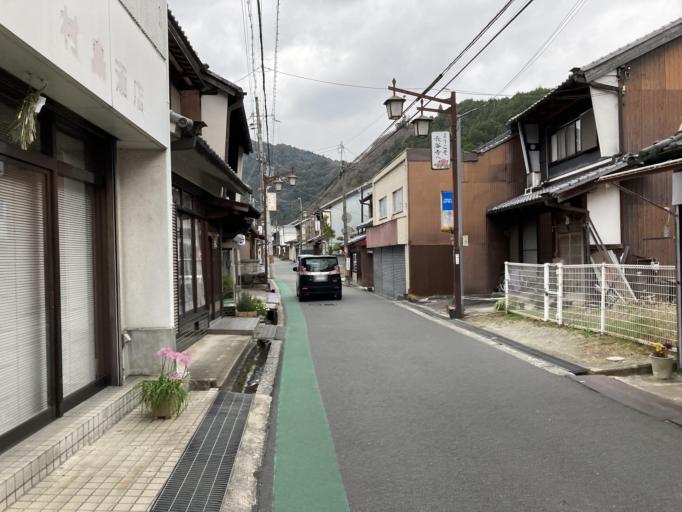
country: JP
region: Nara
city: Haibara-akanedai
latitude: 34.5299
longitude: 135.9045
